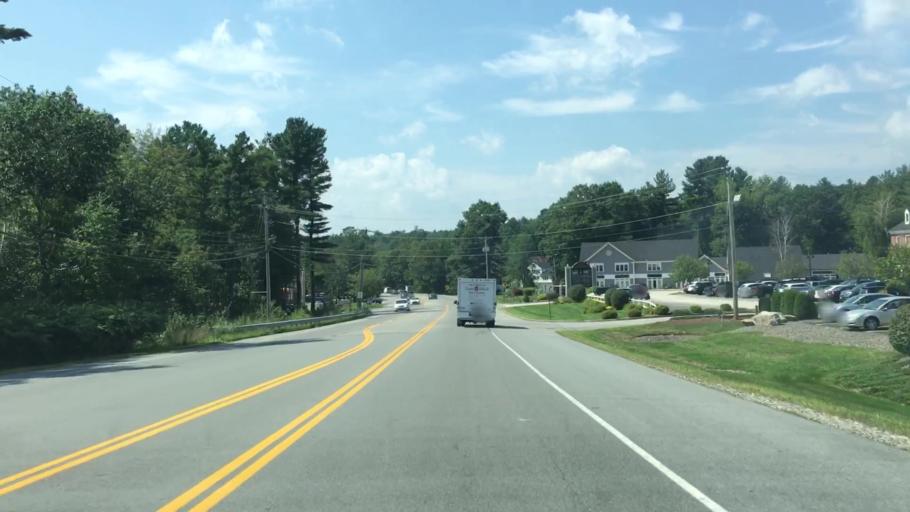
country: US
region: New Hampshire
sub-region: Rockingham County
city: Windham
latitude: 42.8057
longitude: -71.2946
